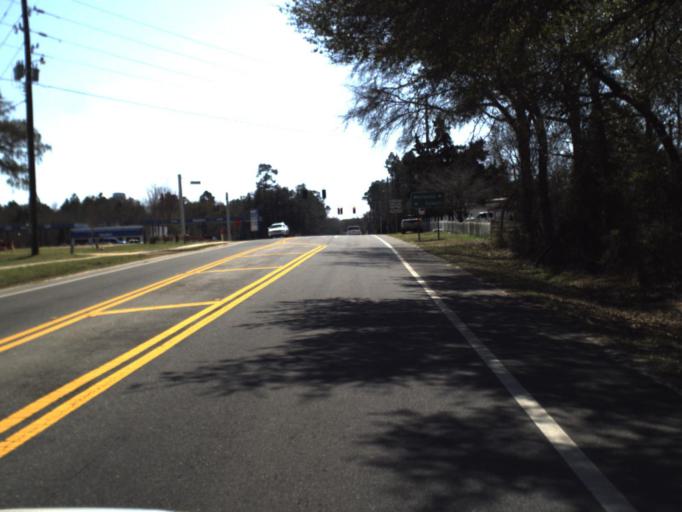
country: US
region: Florida
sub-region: Jackson County
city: Sneads
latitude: 30.7207
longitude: -85.0202
